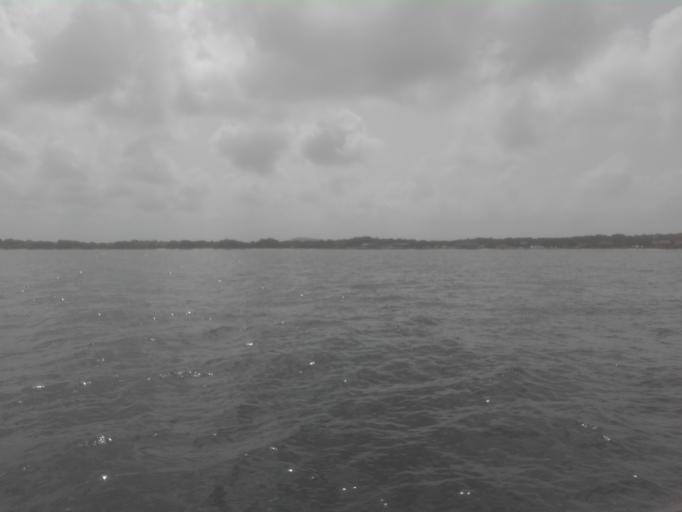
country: CO
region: Bolivar
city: Turbana
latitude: 10.2302
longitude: -75.6113
